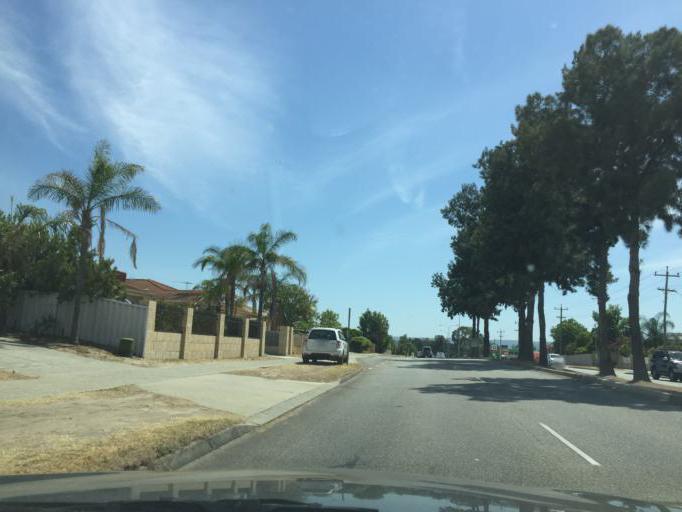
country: AU
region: Western Australia
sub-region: Gosnells
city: Thornlie
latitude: -32.0726
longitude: 115.9644
